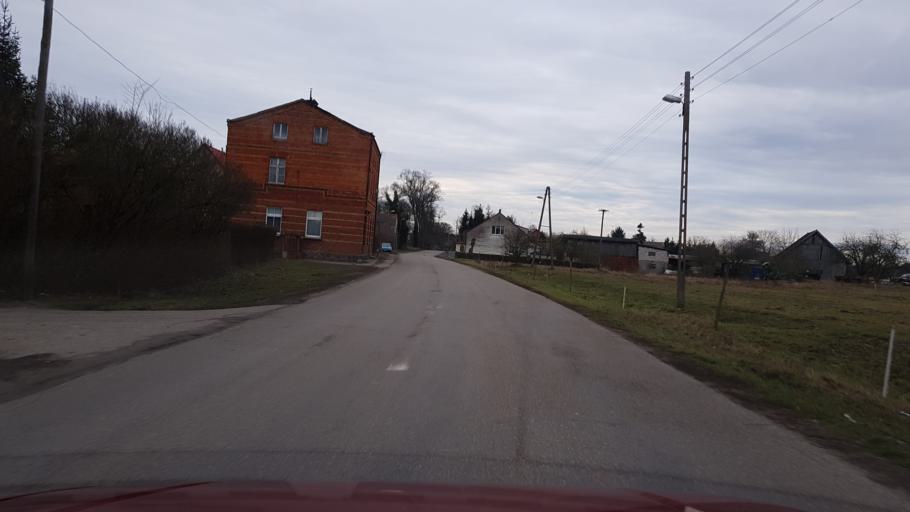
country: PL
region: West Pomeranian Voivodeship
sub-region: Powiat policki
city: Dobra
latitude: 53.5481
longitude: 14.4607
